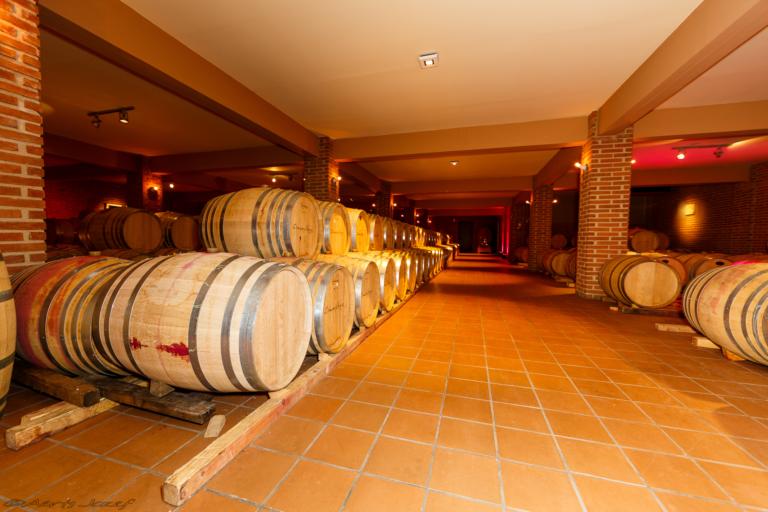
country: GR
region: Peloponnese
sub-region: Nomos Argolidos
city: Koutsopodi
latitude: 37.6888
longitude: 22.6543
